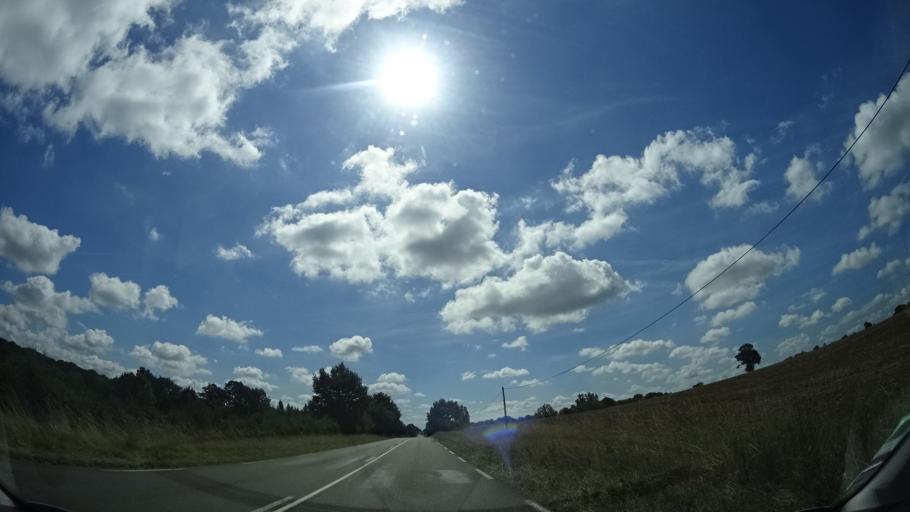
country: FR
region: Pays de la Loire
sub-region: Departement de la Mayenne
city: Meslay-du-Maine
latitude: 47.9235
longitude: -0.4826
